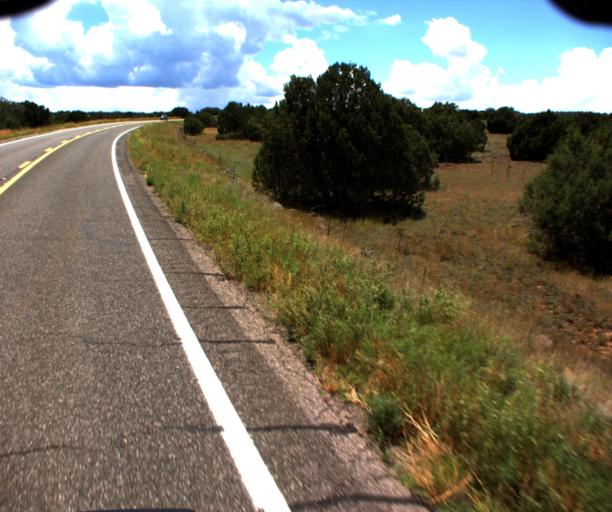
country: US
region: Arizona
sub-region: Gila County
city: Pine
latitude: 34.4890
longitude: -111.5977
